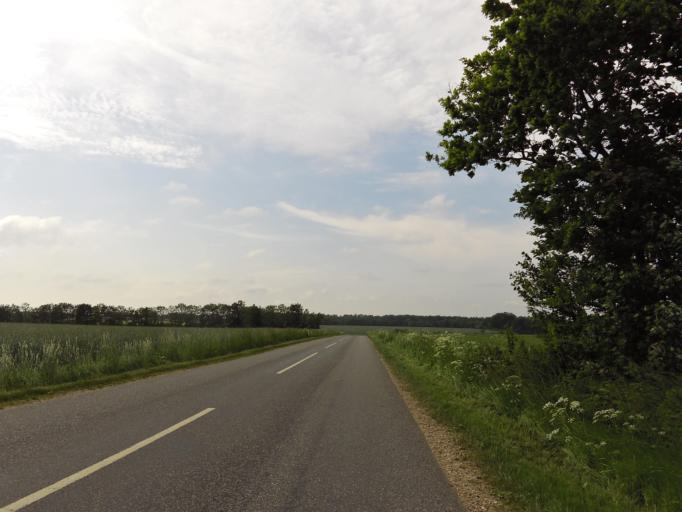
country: DK
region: South Denmark
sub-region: Haderslev Kommune
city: Gram
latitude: 55.2834
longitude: 9.0869
